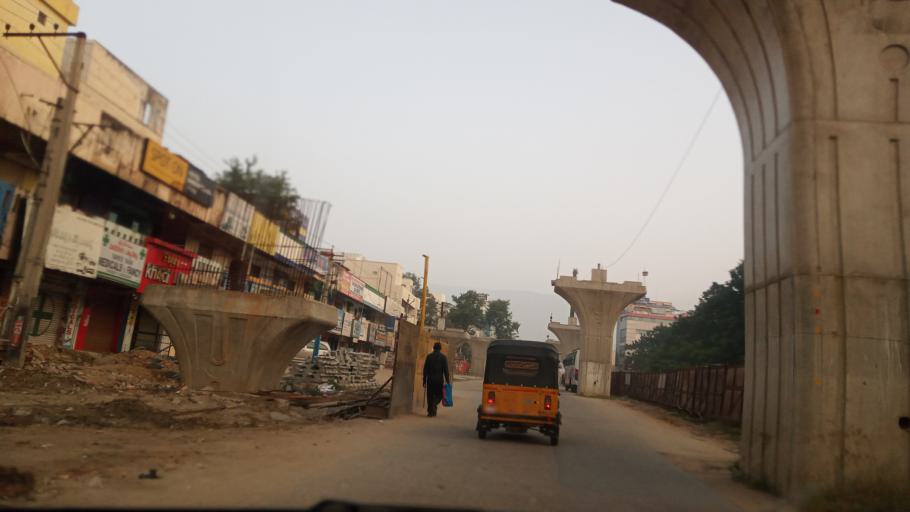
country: IN
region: Andhra Pradesh
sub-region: Chittoor
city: Tirupati
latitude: 13.6325
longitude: 79.4279
